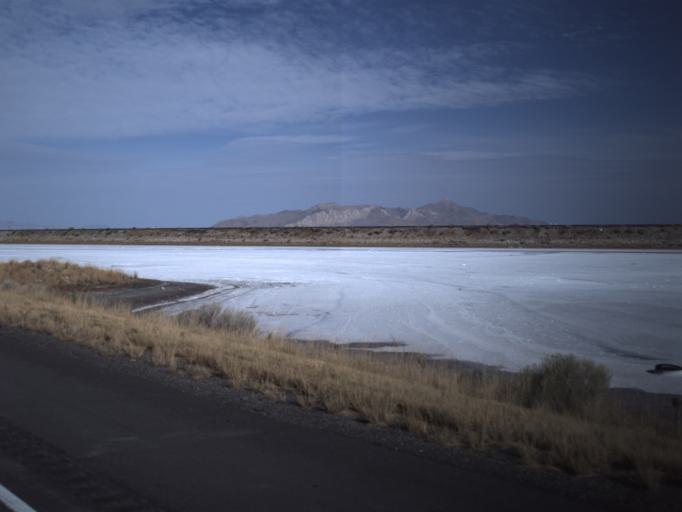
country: US
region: Utah
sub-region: Tooele County
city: Stansbury park
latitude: 40.6658
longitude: -112.3671
